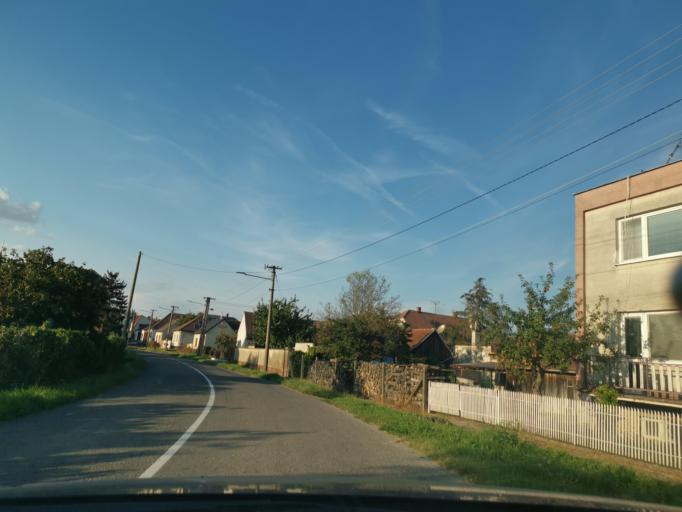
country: SK
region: Trnavsky
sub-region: Okres Senica
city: Senica
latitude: 48.6749
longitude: 17.2575
